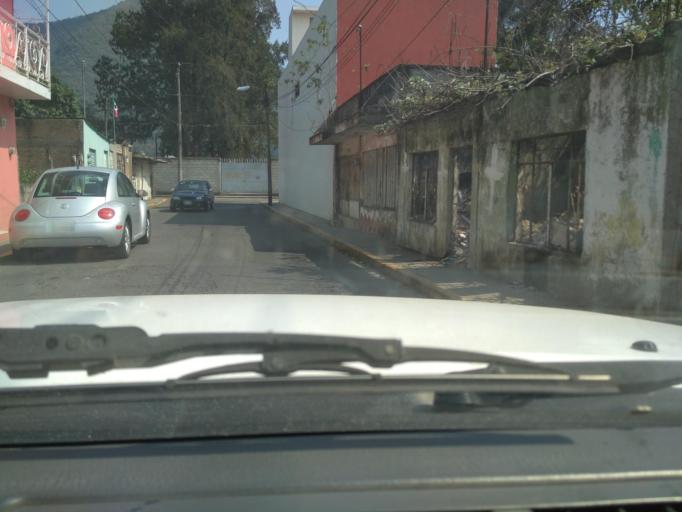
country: MX
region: Veracruz
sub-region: Mariano Escobedo
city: Palmira
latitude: 18.8744
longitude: -97.0986
